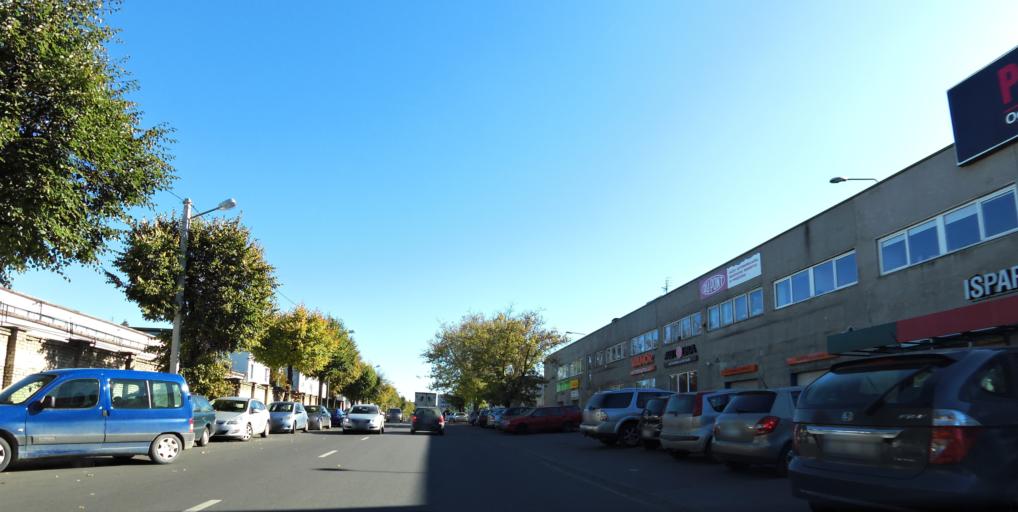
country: LT
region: Vilnius County
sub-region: Vilnius
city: Vilnius
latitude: 54.7151
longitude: 25.2982
